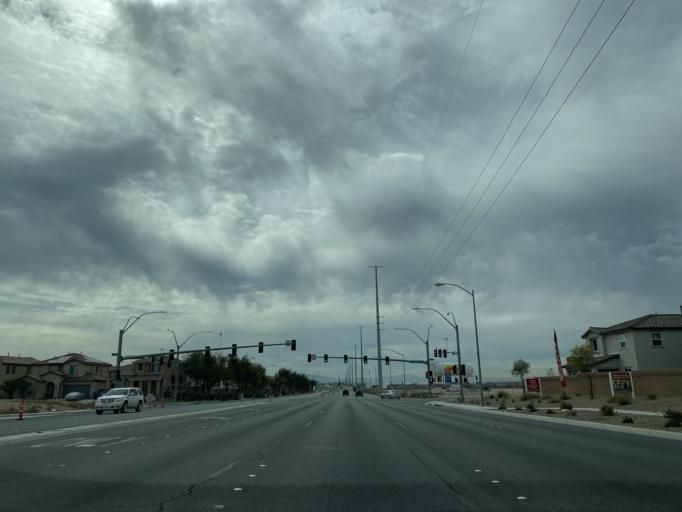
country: US
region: Nevada
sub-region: Clark County
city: Nellis Air Force Base
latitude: 36.2739
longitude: -115.0800
